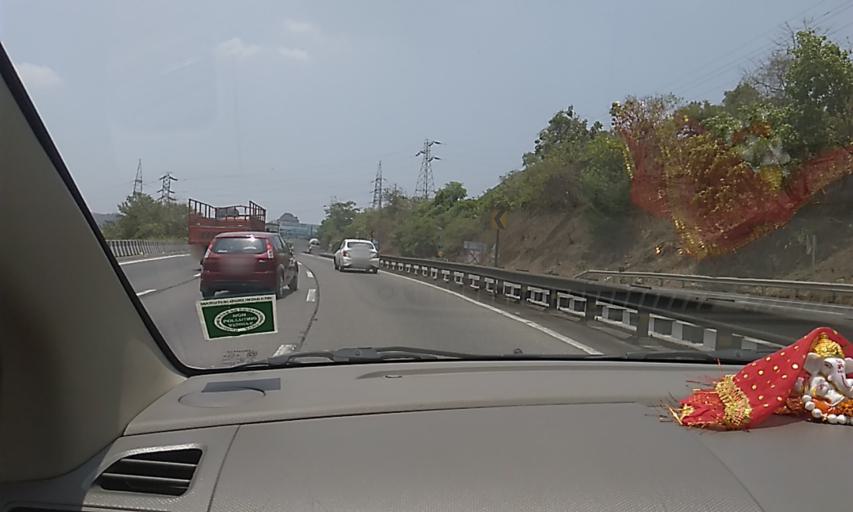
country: IN
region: Maharashtra
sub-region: Raigarh
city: Khopoli
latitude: 18.7691
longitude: 73.3578
